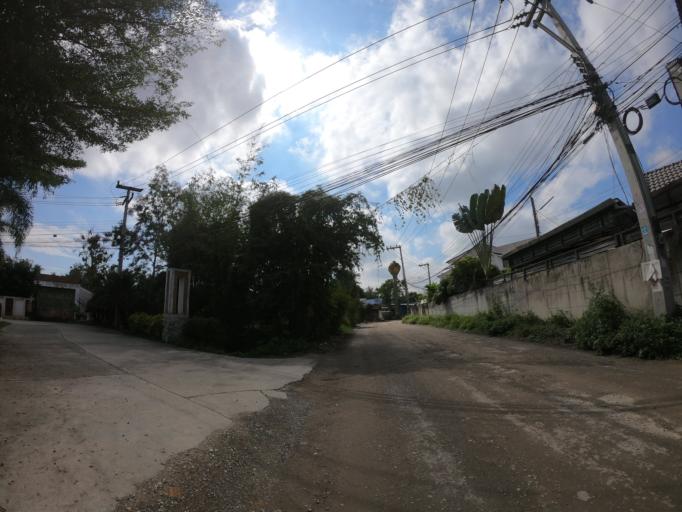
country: TH
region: Chiang Mai
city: San Sai
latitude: 18.8219
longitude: 99.0580
